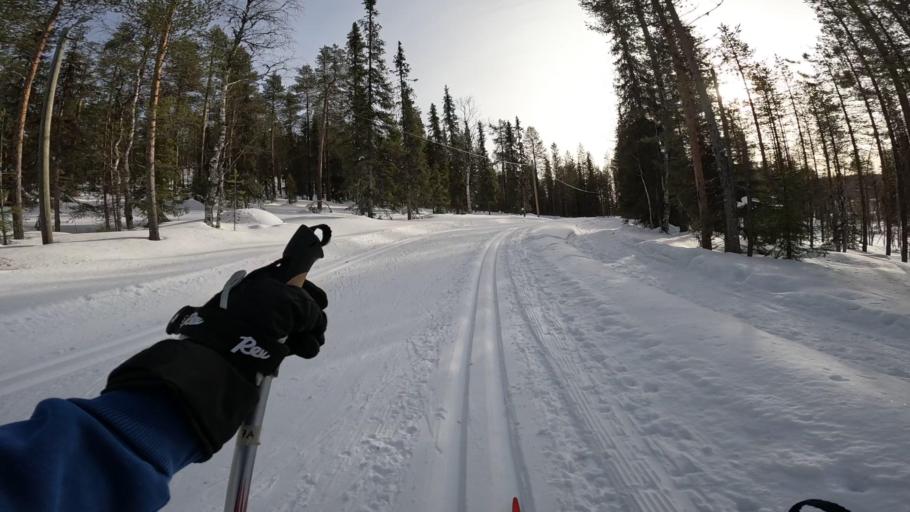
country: FI
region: Lapland
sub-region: Itae-Lappi
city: Salla
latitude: 66.7460
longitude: 28.8127
